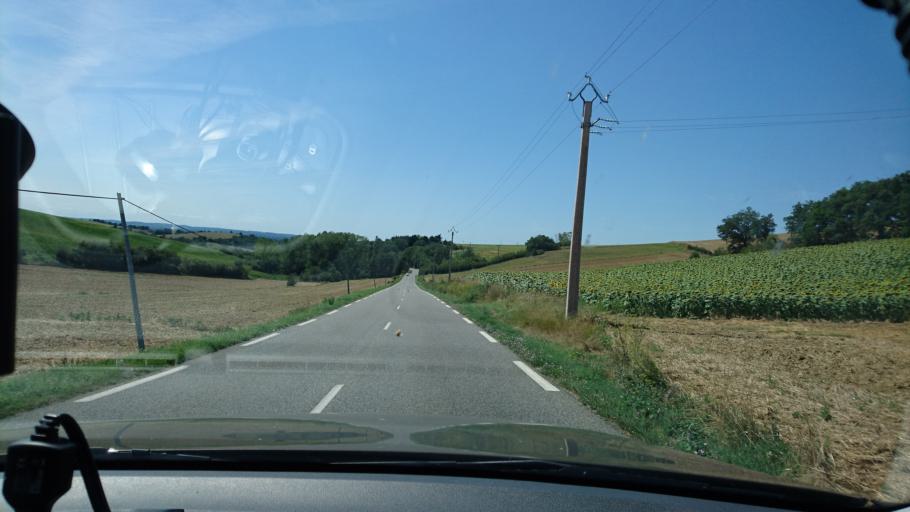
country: FR
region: Midi-Pyrenees
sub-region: Departement de la Haute-Garonne
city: Noe
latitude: 43.3388
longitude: 1.2903
